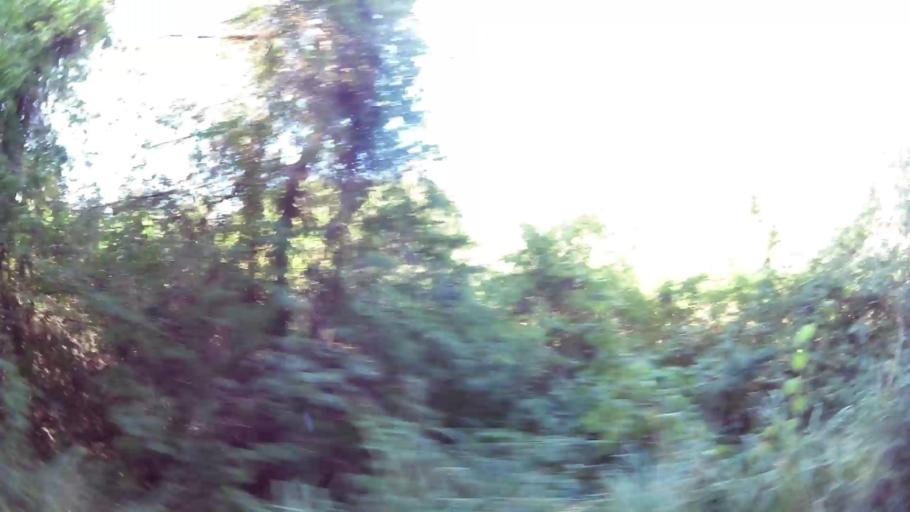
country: VG
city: Road Town
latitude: 18.3926
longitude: -64.7027
